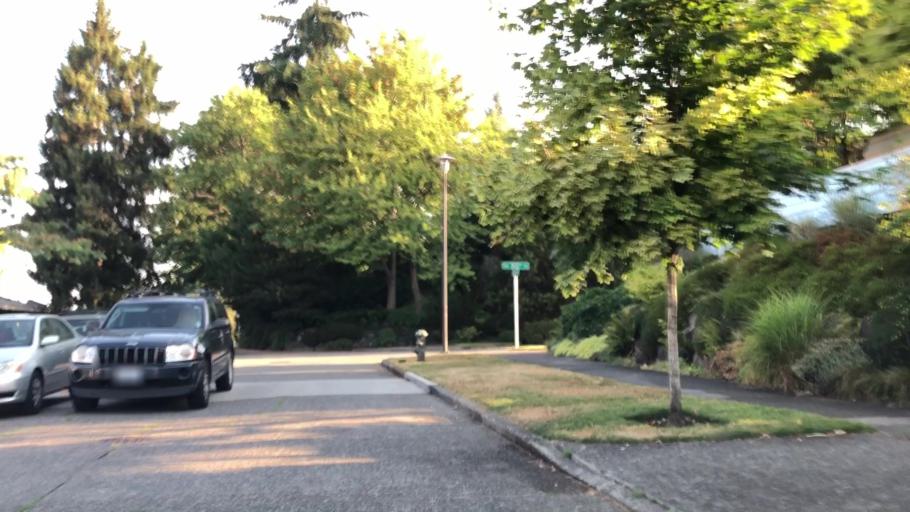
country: US
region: Washington
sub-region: King County
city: Yarrow Point
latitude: 47.6646
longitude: -122.2794
